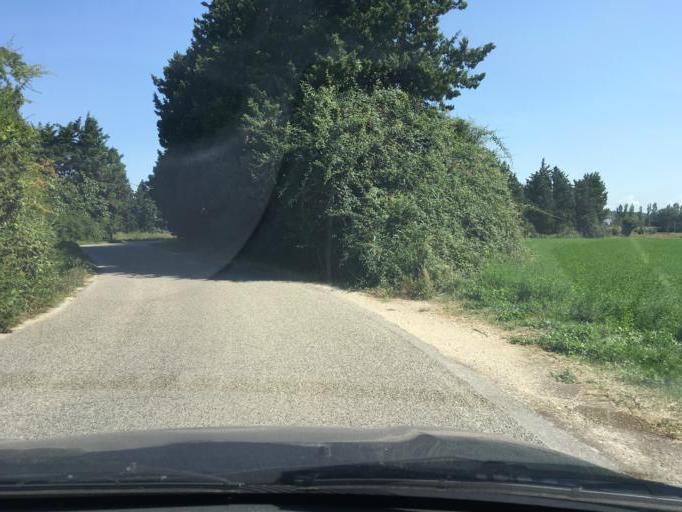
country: FR
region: Provence-Alpes-Cote d'Azur
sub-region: Departement du Vaucluse
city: Orange
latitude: 44.1222
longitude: 4.7848
